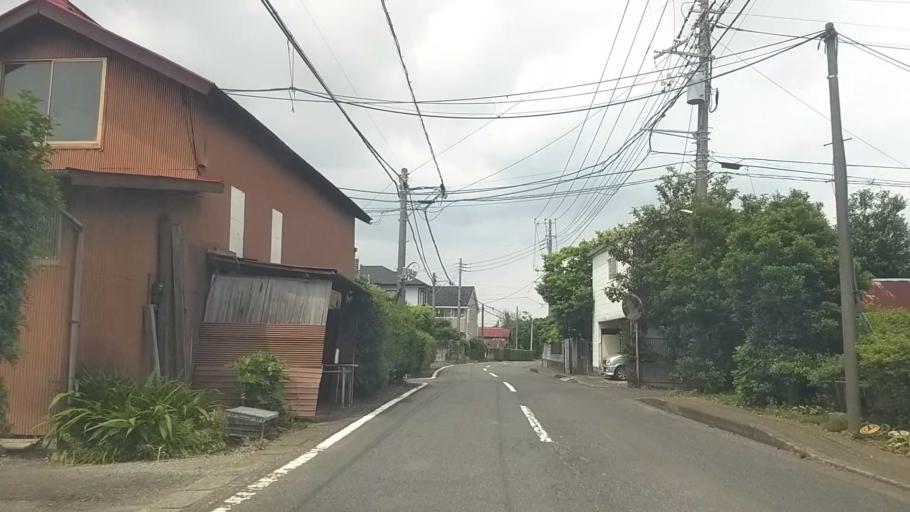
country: JP
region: Kanagawa
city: Chigasaki
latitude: 35.3911
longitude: 139.4144
